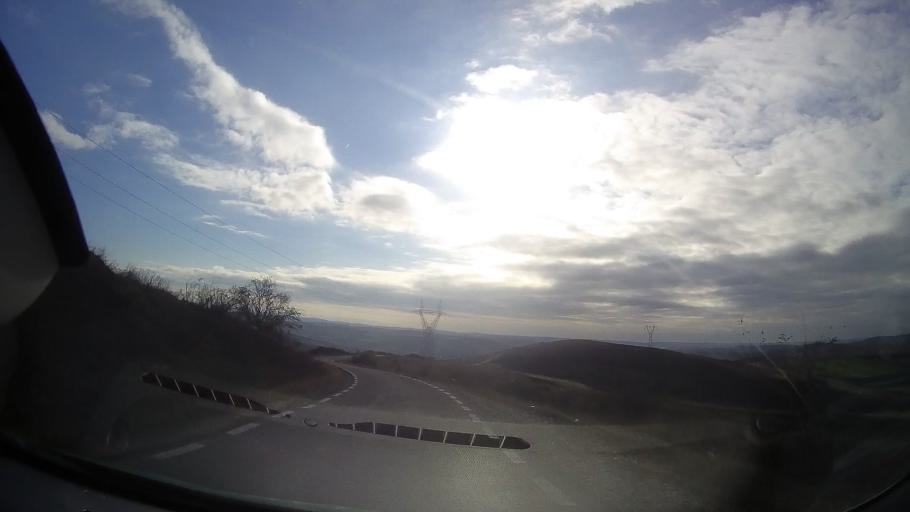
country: RO
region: Mures
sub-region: Comuna Sanger
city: Sanger
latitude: 46.5563
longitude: 24.1602
